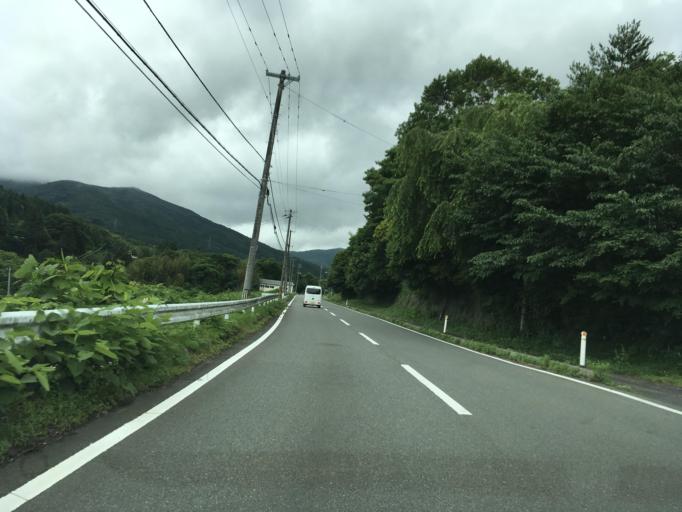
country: JP
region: Iwate
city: Ofunato
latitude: 38.8980
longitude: 141.4882
